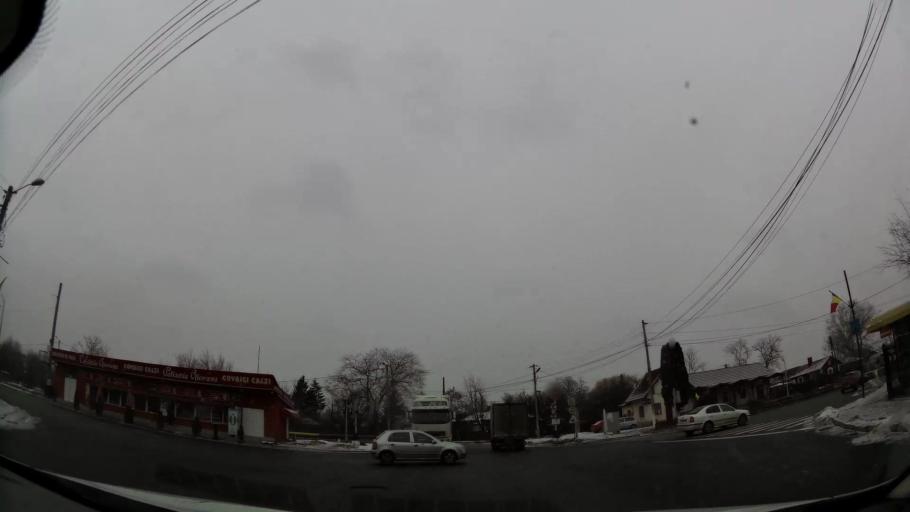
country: RO
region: Dambovita
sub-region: Municipiul Targoviste
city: Targoviste
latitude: 44.9401
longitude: 25.4439
